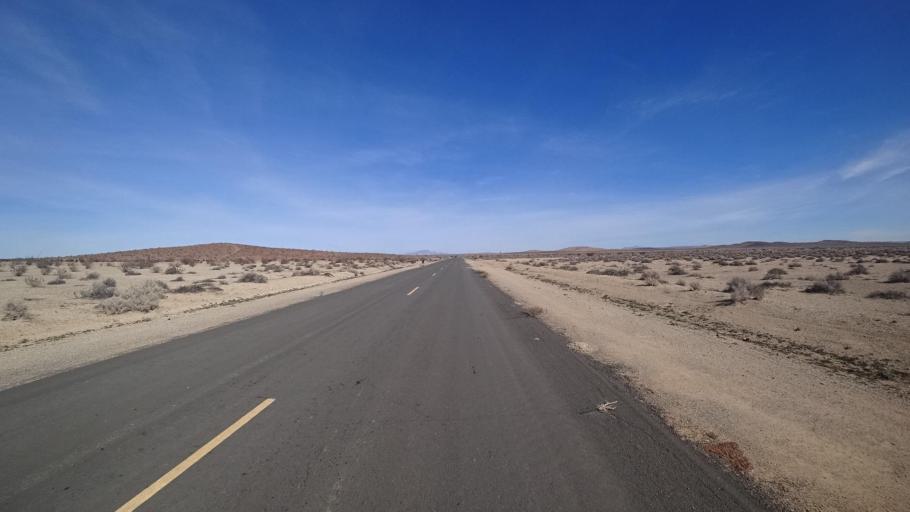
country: US
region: California
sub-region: Kern County
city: North Edwards
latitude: 35.0572
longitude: -117.8100
